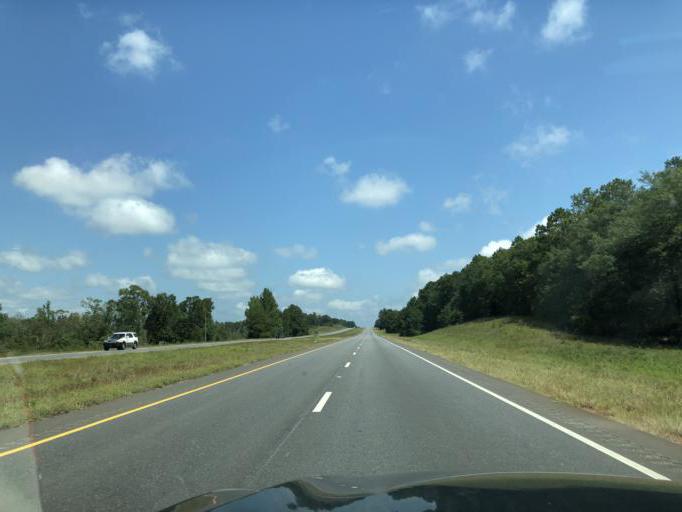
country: US
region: Alabama
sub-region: Henry County
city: Abbeville
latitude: 31.4708
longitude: -85.3038
